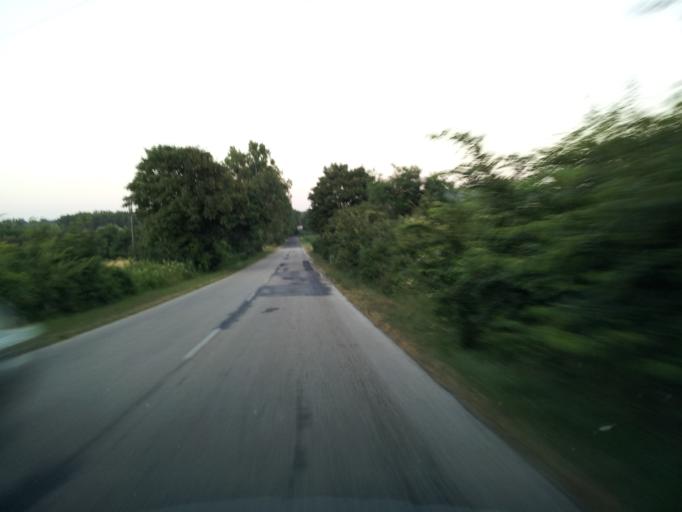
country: HU
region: Fejer
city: Szarliget
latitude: 47.5248
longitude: 18.4726
